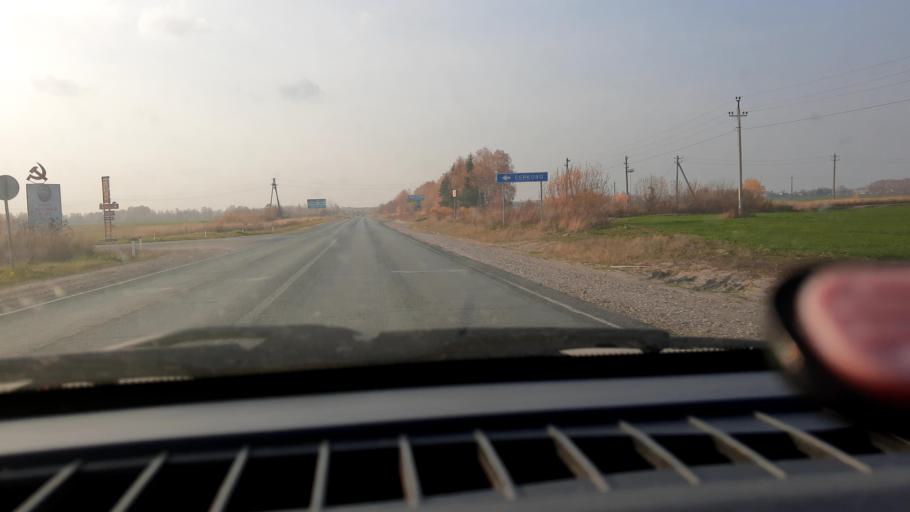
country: RU
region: Nizjnij Novgorod
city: Gorodets
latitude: 56.6384
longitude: 43.5176
